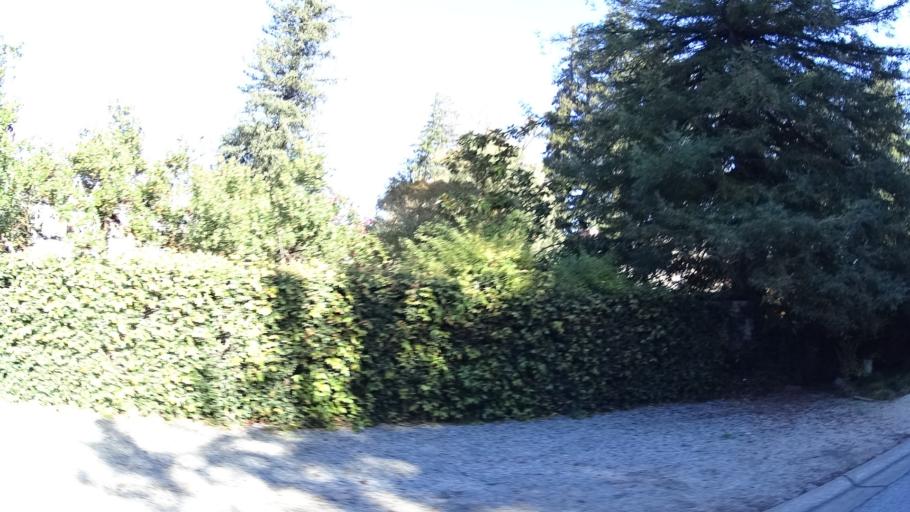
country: US
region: California
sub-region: San Mateo County
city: Burlingame
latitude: 37.5766
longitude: -122.3604
